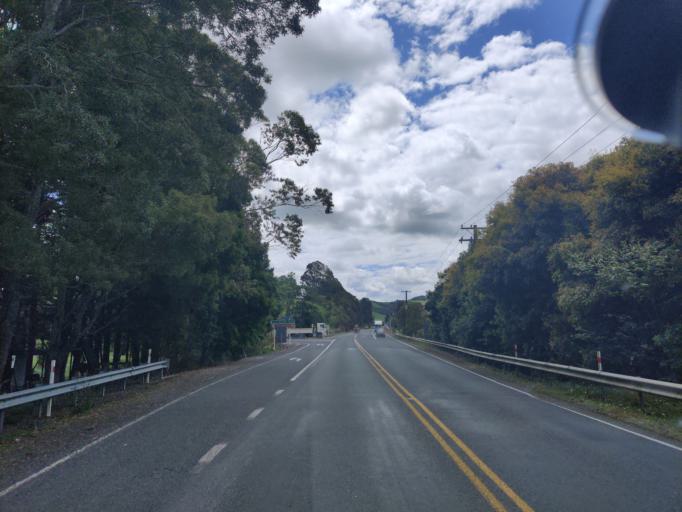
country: NZ
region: Northland
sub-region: Far North District
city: Kerikeri
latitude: -35.3021
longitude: 173.9606
